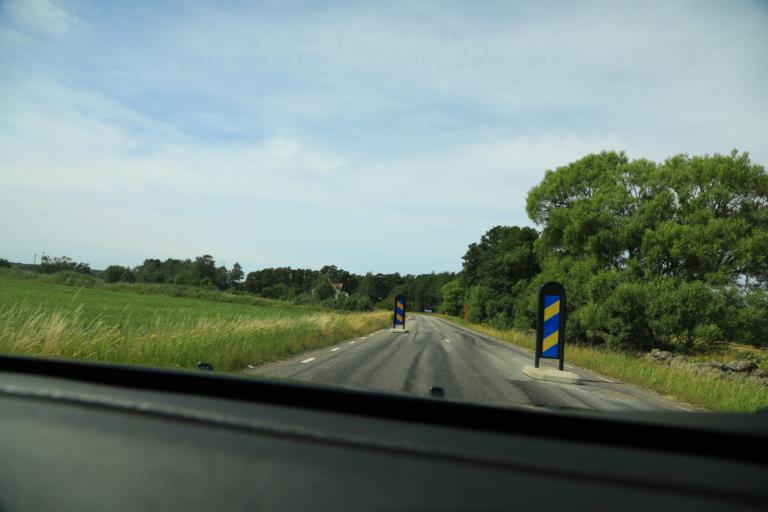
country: SE
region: Halland
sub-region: Varbergs Kommun
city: Varberg
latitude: 57.1443
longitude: 12.2772
